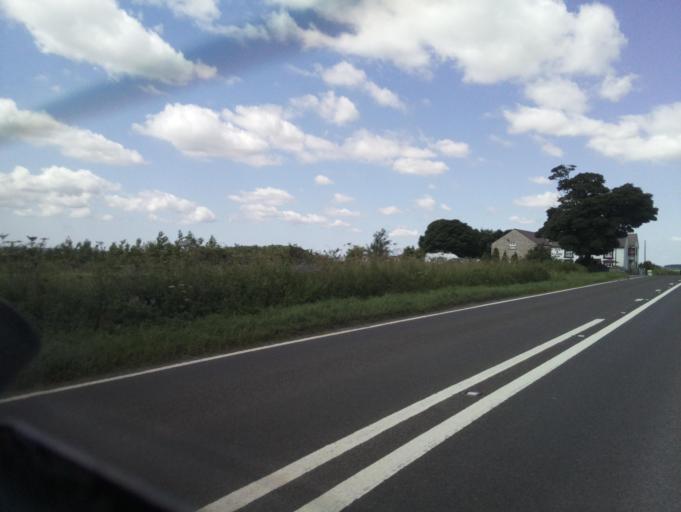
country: GB
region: England
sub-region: Derbyshire
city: Bakewell
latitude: 53.1495
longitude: -1.7664
